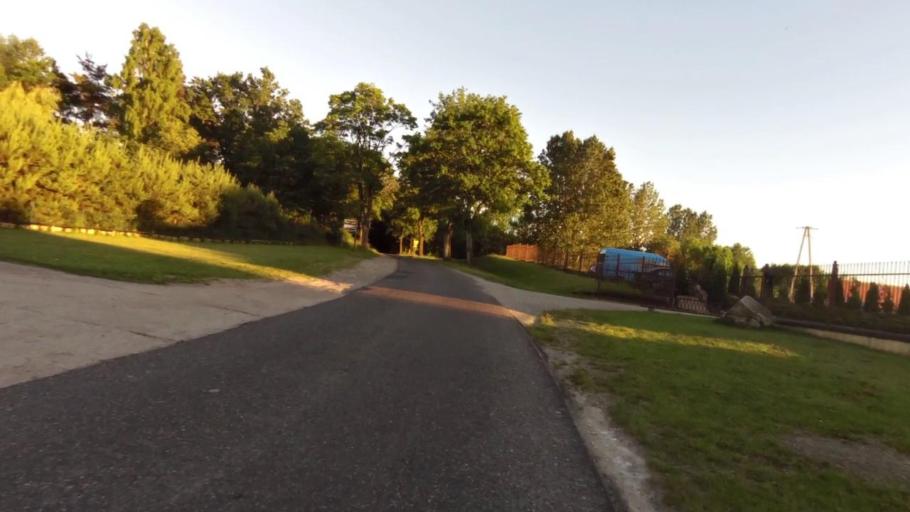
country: PL
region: West Pomeranian Voivodeship
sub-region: Powiat bialogardzki
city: Bialogard
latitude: 54.0405
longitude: 16.0468
